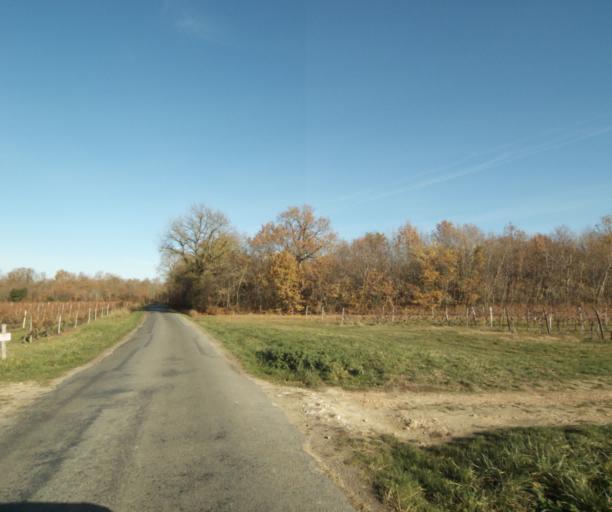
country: FR
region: Poitou-Charentes
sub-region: Departement de la Charente-Maritime
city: Burie
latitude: 45.7715
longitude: -0.4436
